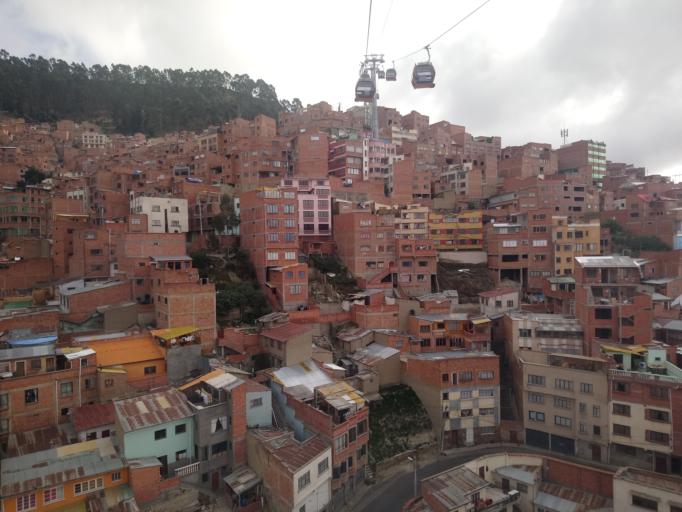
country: BO
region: La Paz
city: La Paz
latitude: -16.4886
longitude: -68.1344
